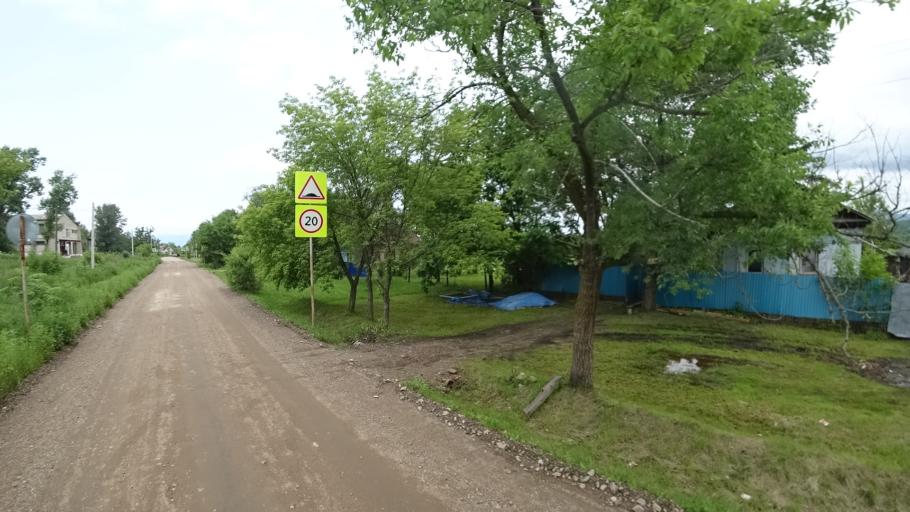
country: RU
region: Primorskiy
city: Novosysoyevka
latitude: 44.2377
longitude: 133.3646
